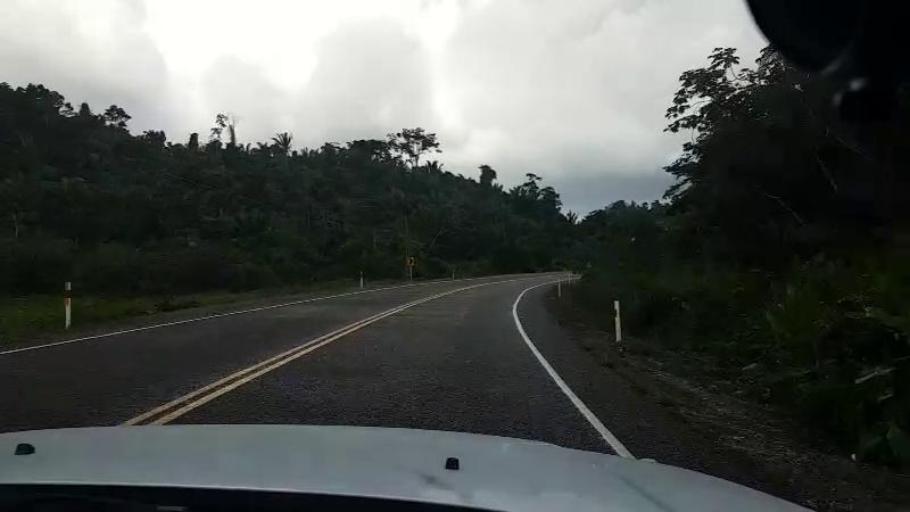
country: BZ
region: Cayo
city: Belmopan
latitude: 17.1578
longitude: -88.6889
